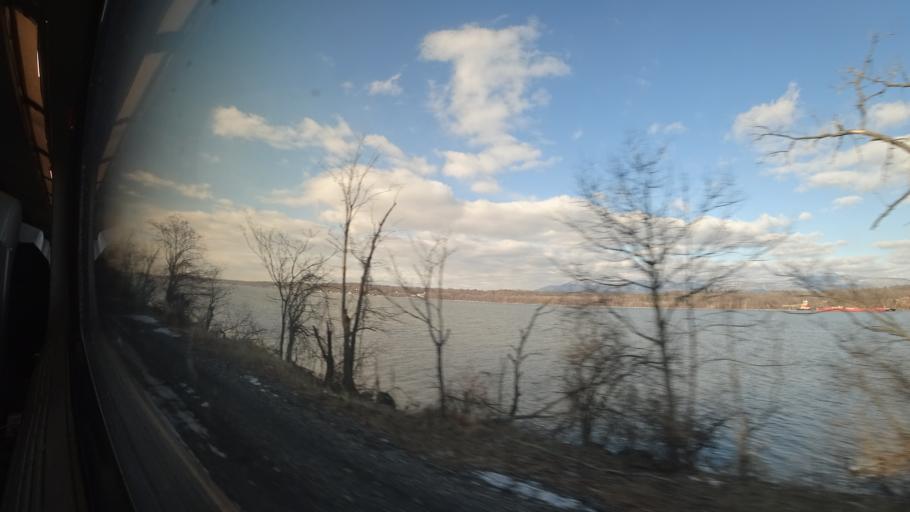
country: US
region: New York
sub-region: Ulster County
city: Saugerties
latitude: 42.1096
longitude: -73.9145
